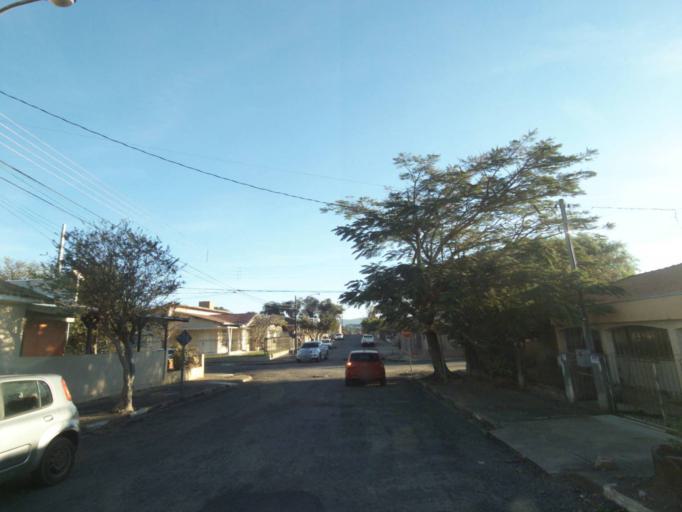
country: BR
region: Parana
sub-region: Tibagi
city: Tibagi
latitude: -24.5165
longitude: -50.4124
